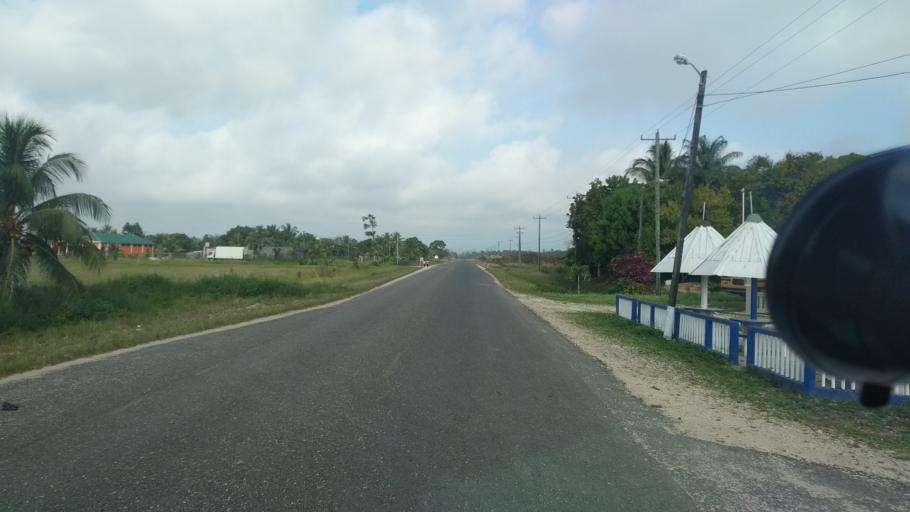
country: BZ
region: Stann Creek
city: Placencia
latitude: 16.5122
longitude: -88.5421
